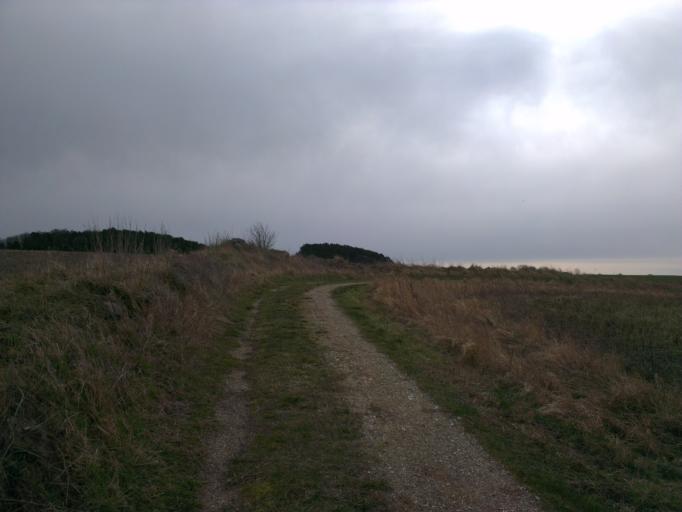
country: DK
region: Zealand
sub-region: Lejre Kommune
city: Ejby
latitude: 55.7717
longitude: 11.8657
